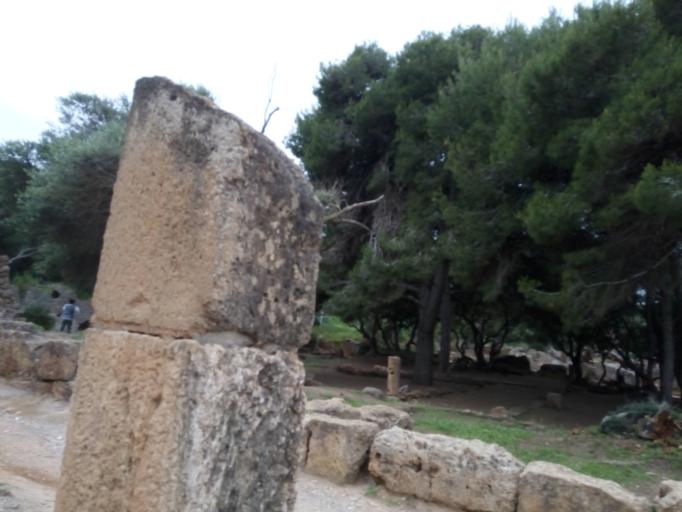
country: DZ
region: Tipaza
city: Tipasa
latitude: 36.5943
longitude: 2.4441
